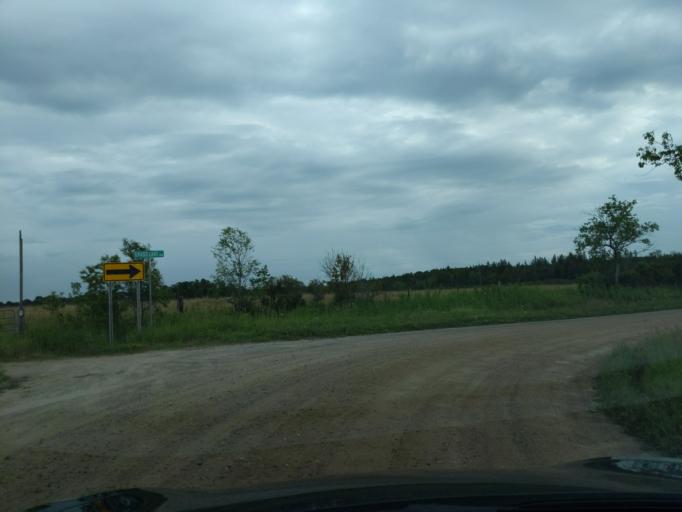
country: US
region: Michigan
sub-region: Clare County
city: Harrison
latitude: 43.9878
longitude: -84.9986
